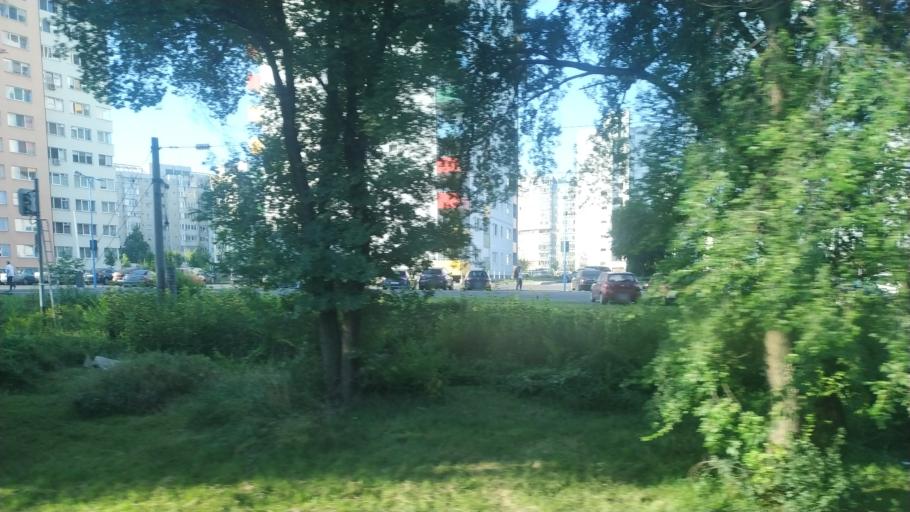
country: RO
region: Brasov
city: Brasov
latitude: 45.6606
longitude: 25.6212
